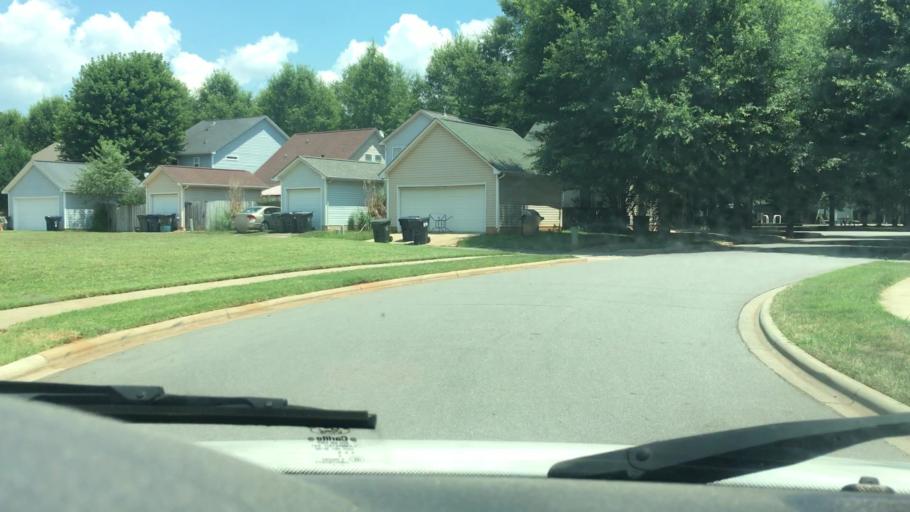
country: US
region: North Carolina
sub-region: Mecklenburg County
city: Huntersville
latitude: 35.3930
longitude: -80.8747
